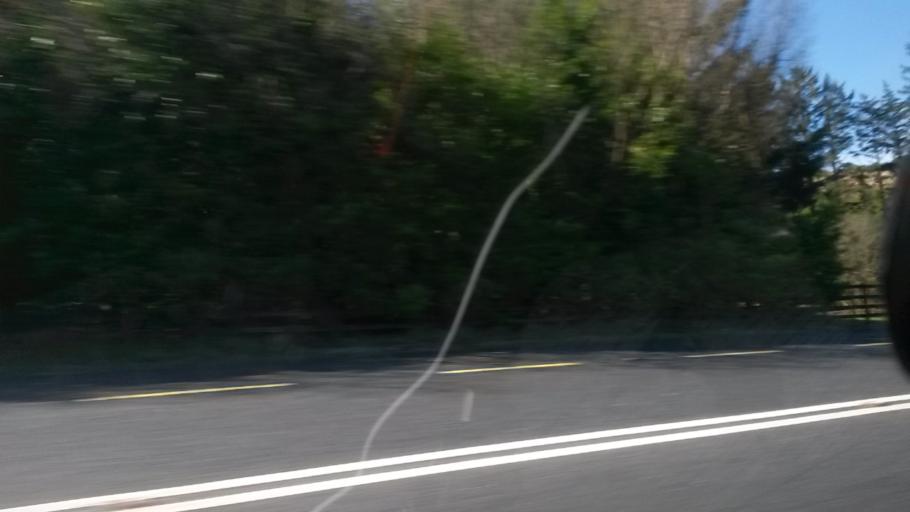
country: IE
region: Munster
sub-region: County Cork
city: Millstreet
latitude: 51.9821
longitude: -9.2762
